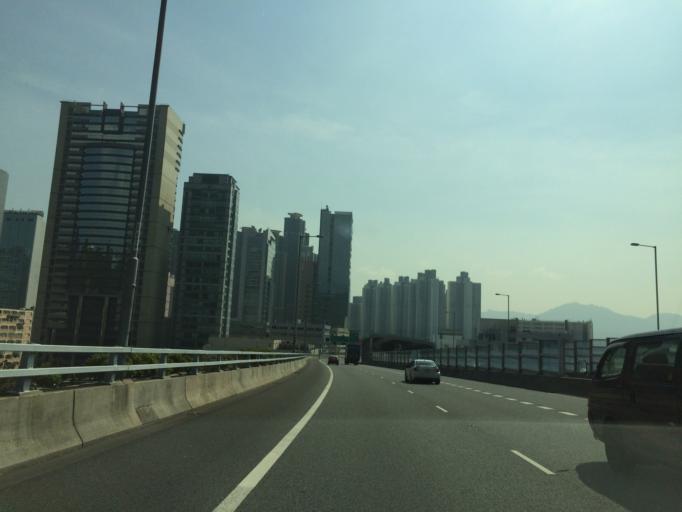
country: HK
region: Sham Shui Po
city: Sham Shui Po
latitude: 22.3404
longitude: 114.1437
